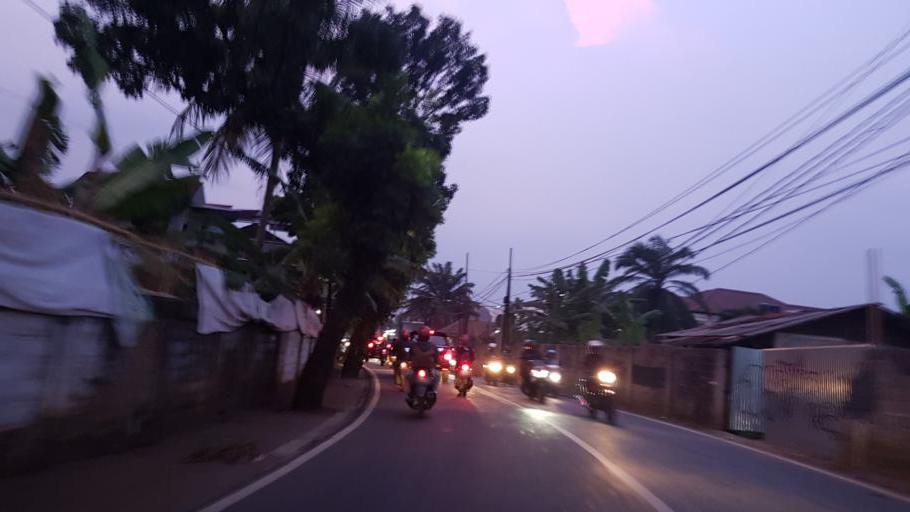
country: ID
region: West Java
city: Depok
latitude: -6.3545
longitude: 106.8012
